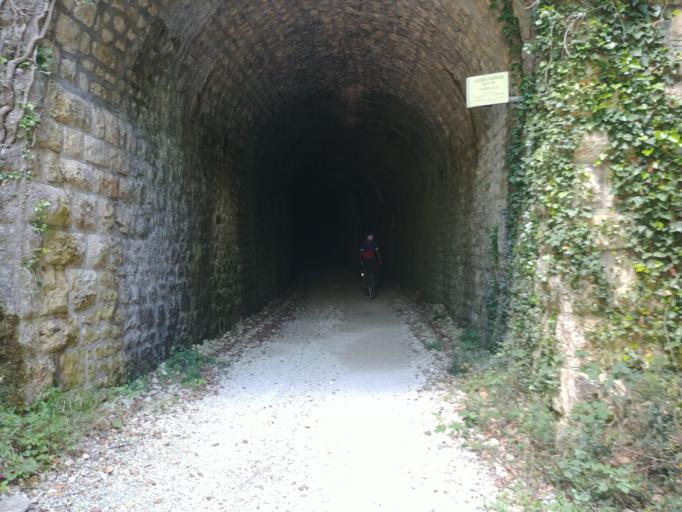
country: IT
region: Umbria
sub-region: Provincia di Perugia
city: Sant'Anatolia di Narco
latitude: 42.7413
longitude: 12.8201
